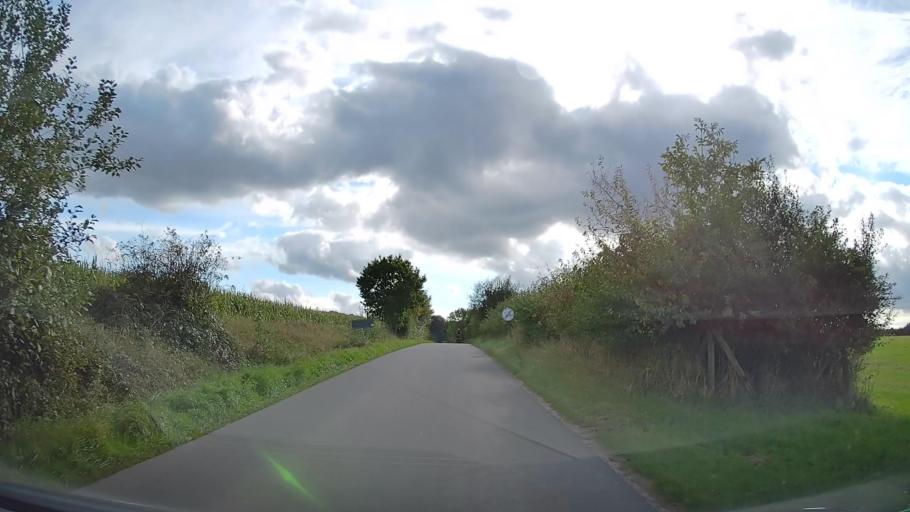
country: DE
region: Schleswig-Holstein
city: Steinberg
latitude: 54.7912
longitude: 9.7798
